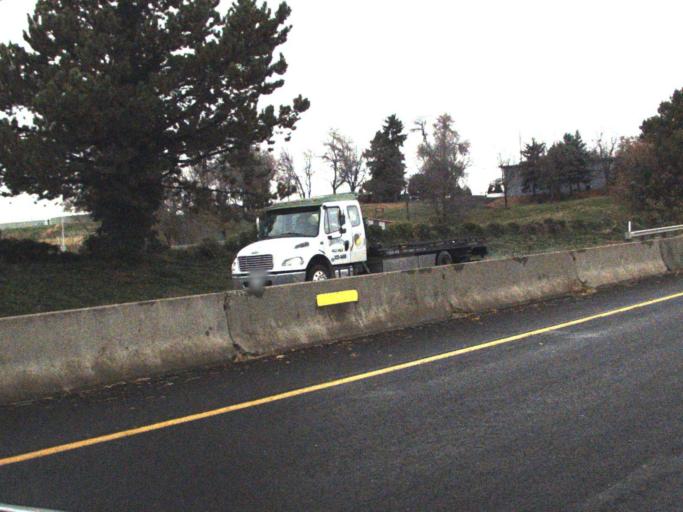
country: US
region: Washington
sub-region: Walla Walla County
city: Walla Walla
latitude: 46.0761
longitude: -118.3385
